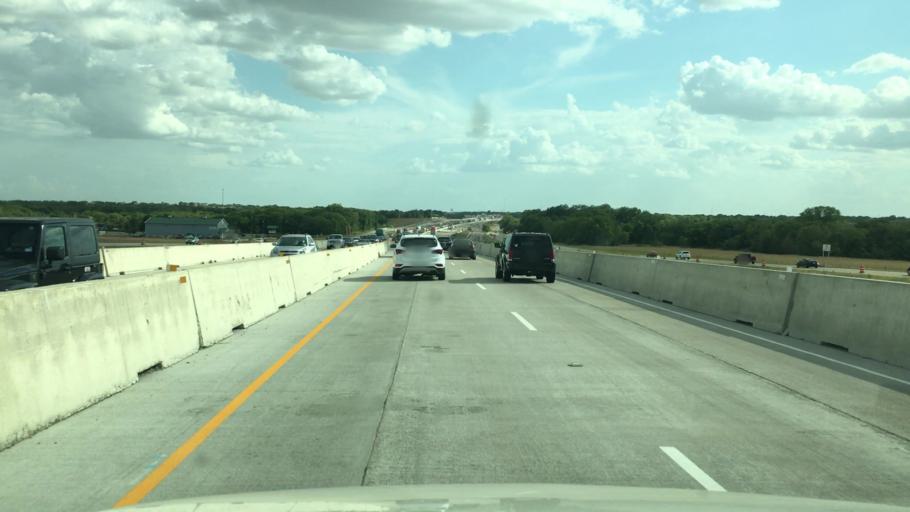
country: US
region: Texas
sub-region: Bell County
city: Troy
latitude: 31.2326
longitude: -97.2890
